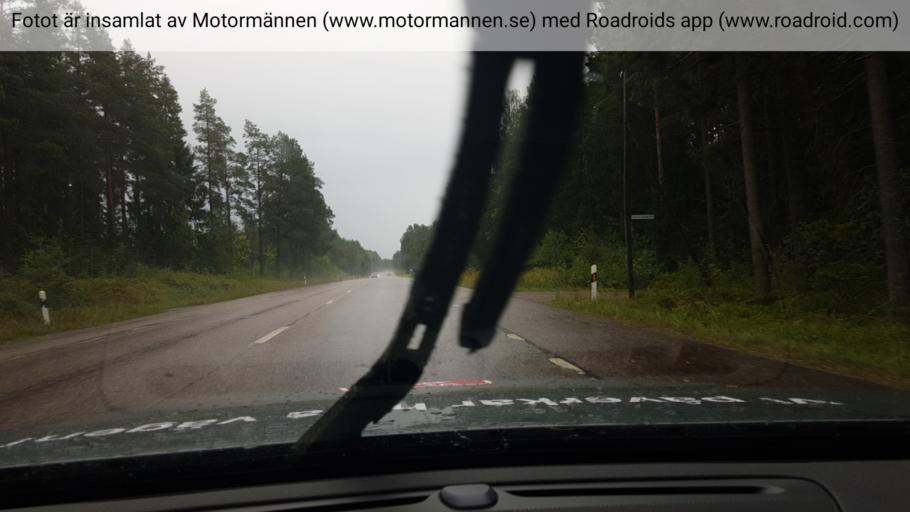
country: SE
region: Uppsala
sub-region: Alvkarleby Kommun
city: AElvkarleby
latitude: 60.5954
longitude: 17.4620
